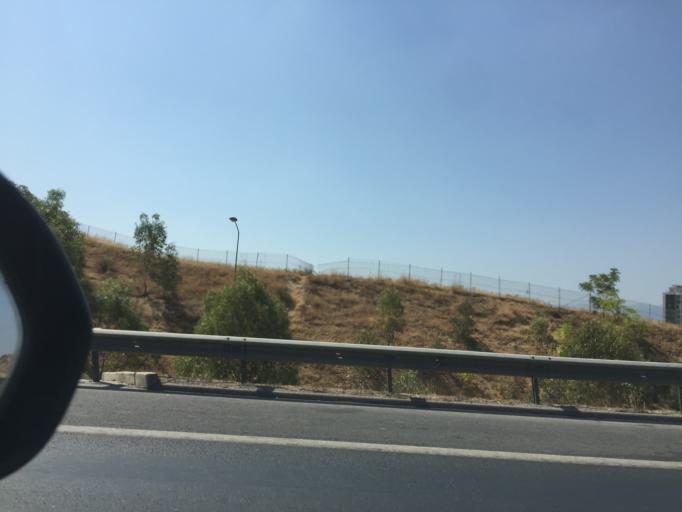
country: TR
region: Izmir
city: Karsiyaka
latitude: 38.4860
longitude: 27.1334
